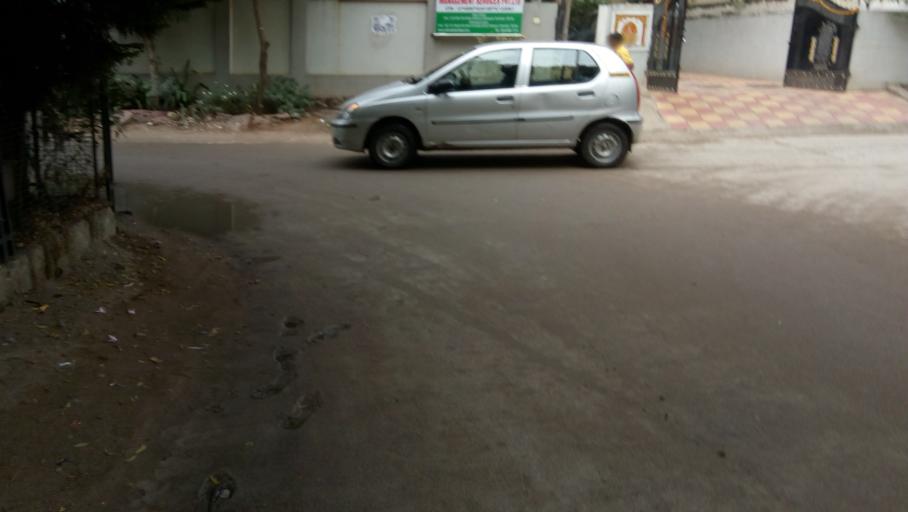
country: IN
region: Telangana
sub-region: Rangareddi
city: Kukatpalli
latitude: 17.4460
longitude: 78.3876
